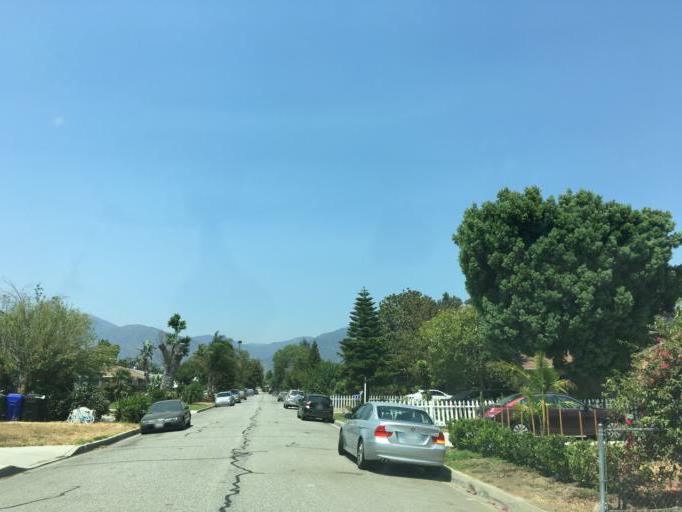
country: US
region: California
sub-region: Los Angeles County
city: Mayflower Village
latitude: 34.1112
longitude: -118.0140
